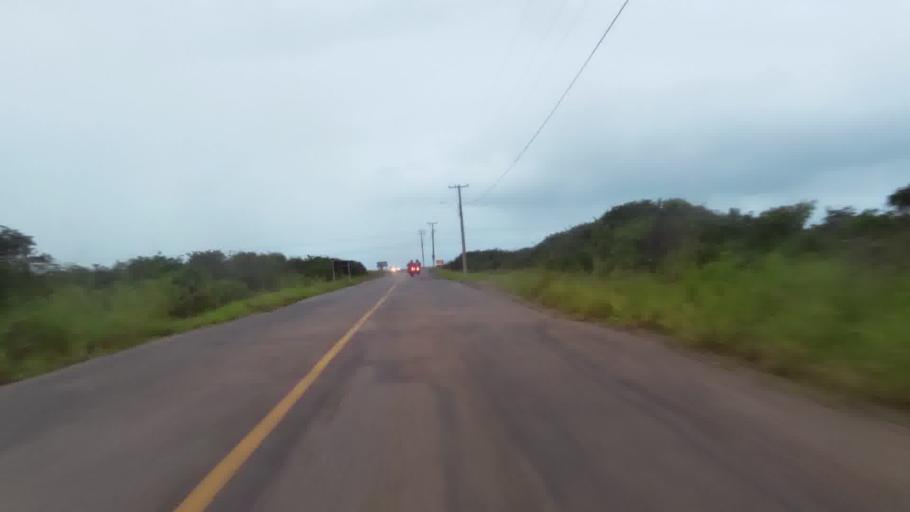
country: BR
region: Espirito Santo
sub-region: Itapemirim
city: Itapemirim
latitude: -20.9794
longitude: -40.8132
